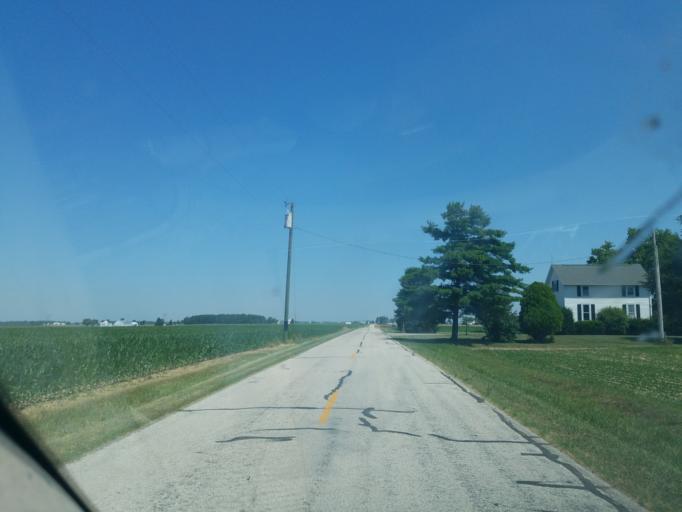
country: US
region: Ohio
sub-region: Mercer County
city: Rockford
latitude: 40.6011
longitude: -84.7085
